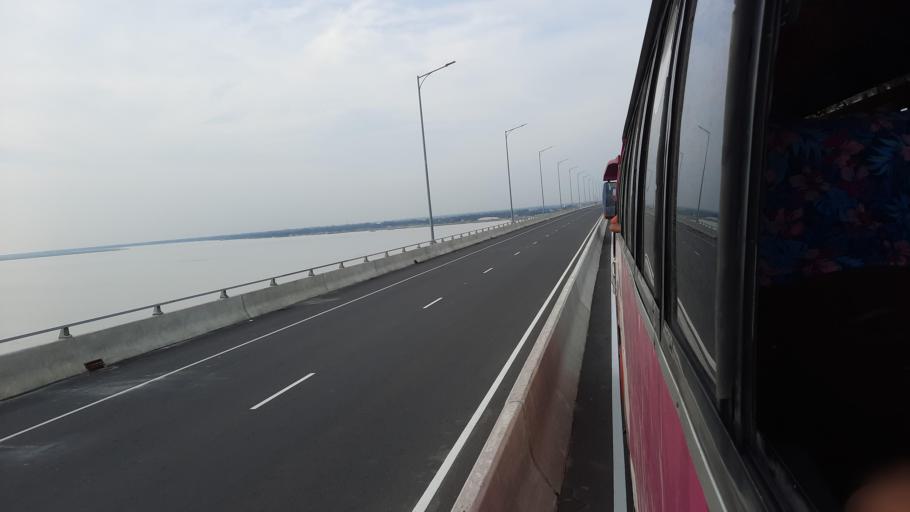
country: BD
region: Dhaka
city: Char Bhadrasan
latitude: 23.4528
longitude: 90.2617
